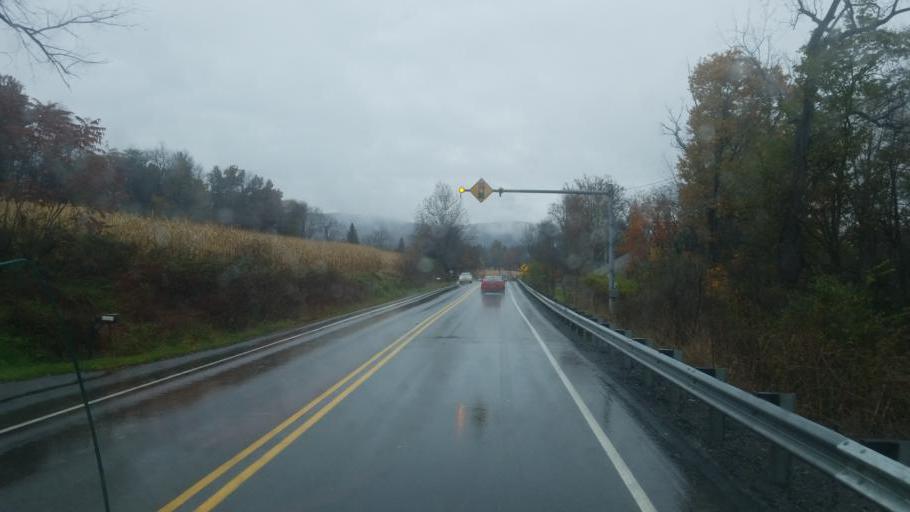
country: US
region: Pennsylvania
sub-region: Clinton County
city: Mill Hall
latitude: 41.1089
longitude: -77.5055
